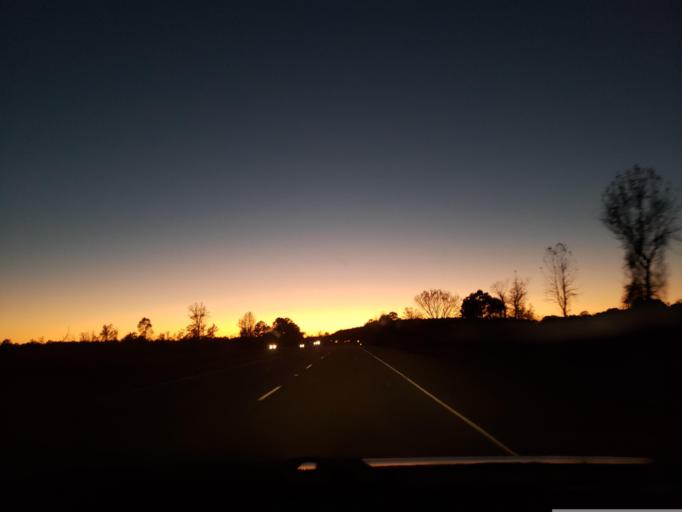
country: US
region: North Carolina
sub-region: Duplin County
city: Kenansville
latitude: 34.9299
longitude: -78.0028
